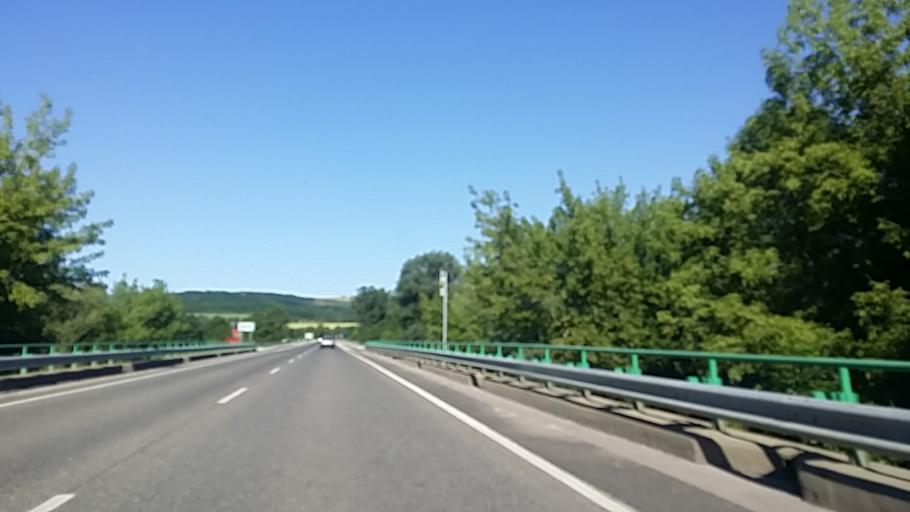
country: HU
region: Zala
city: Heviz
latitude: 46.8019
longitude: 17.1160
